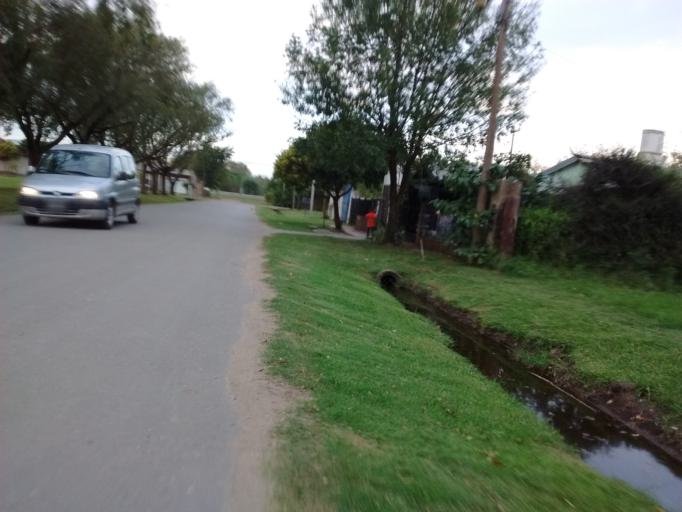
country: AR
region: Santa Fe
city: Granadero Baigorria
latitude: -32.8524
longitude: -60.7846
